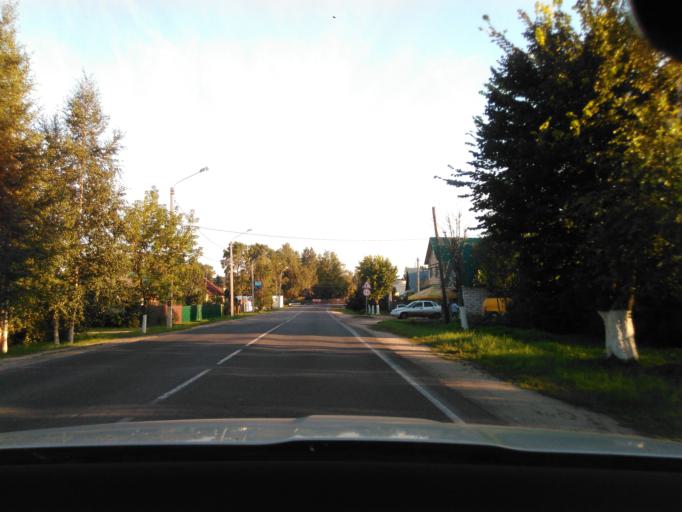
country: RU
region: Tverskaya
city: Konakovo
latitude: 56.6822
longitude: 36.7611
